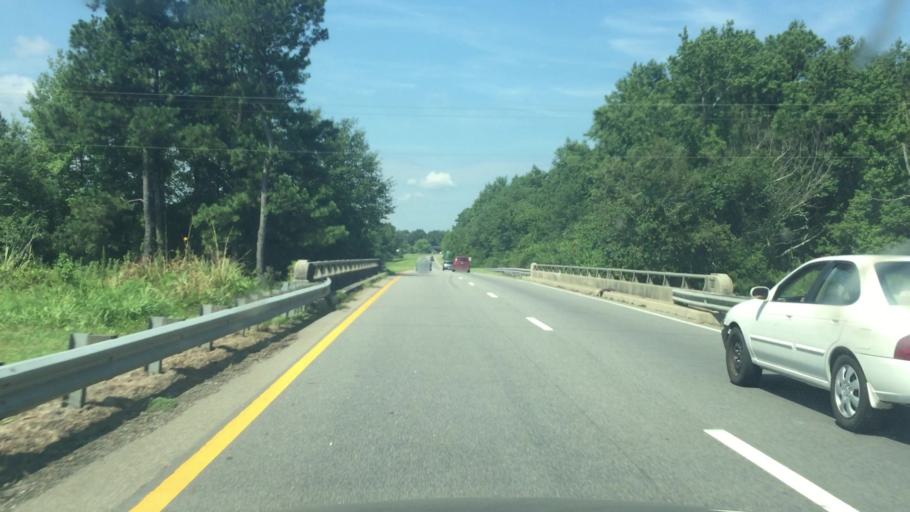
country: US
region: North Carolina
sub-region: Scotland County
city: Laurinburg
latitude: 34.7565
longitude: -79.4362
